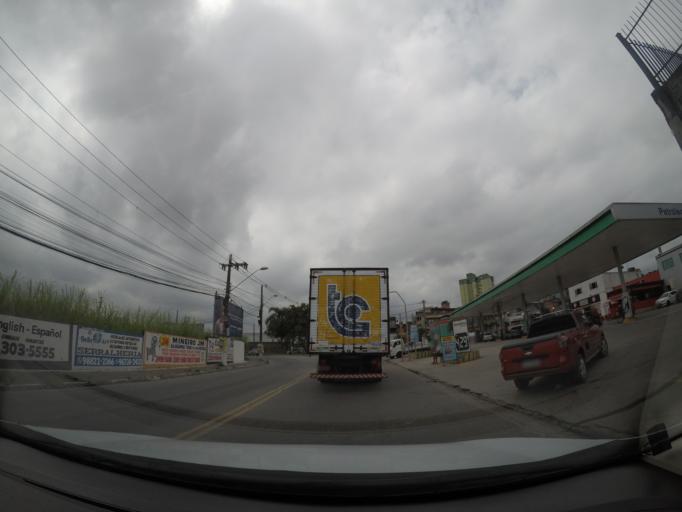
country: BR
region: Sao Paulo
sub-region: Itaquaquecetuba
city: Itaquaquecetuba
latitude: -23.4318
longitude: -46.4023
